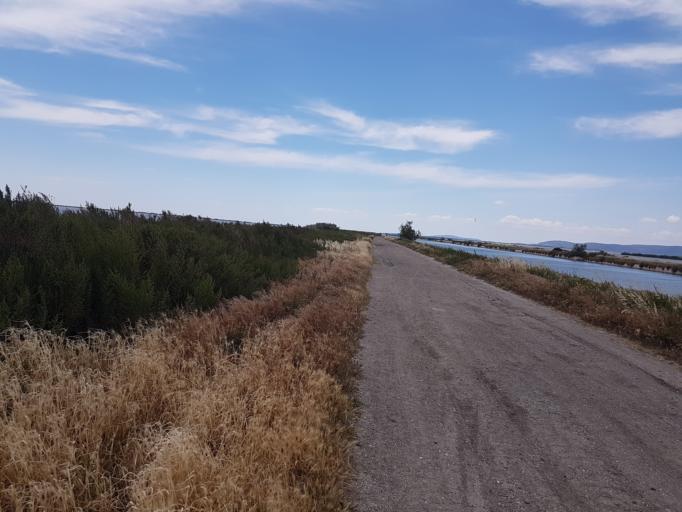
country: FR
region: Languedoc-Roussillon
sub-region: Departement de l'Herault
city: Villeneuve-les-Maguelone
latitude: 43.5107
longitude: 3.8724
